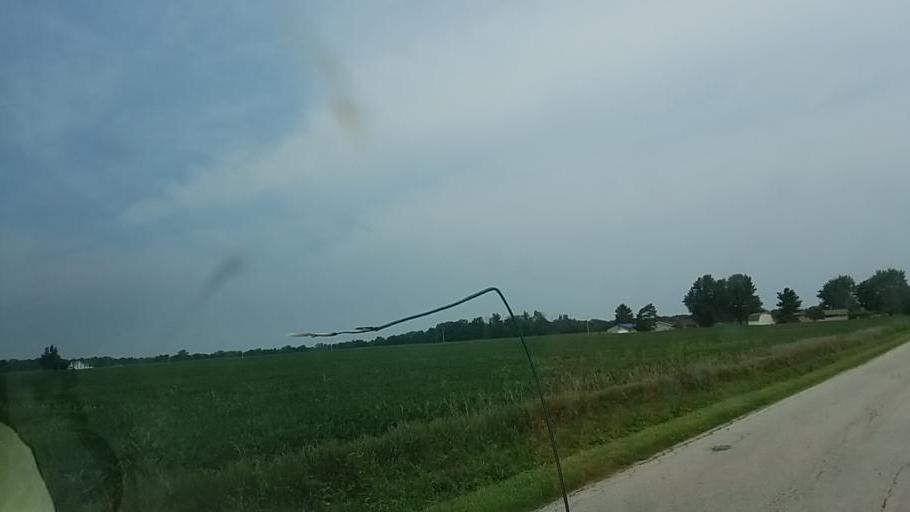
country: US
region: Ohio
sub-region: Morrow County
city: Mount Gilead
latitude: 40.6134
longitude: -82.9184
